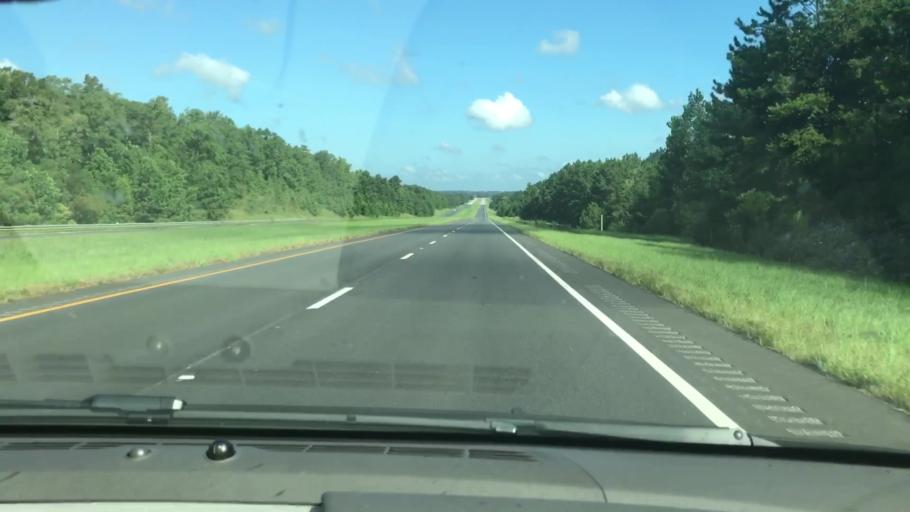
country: US
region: Alabama
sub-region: Barbour County
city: Eufaula
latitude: 32.0485
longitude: -85.1322
